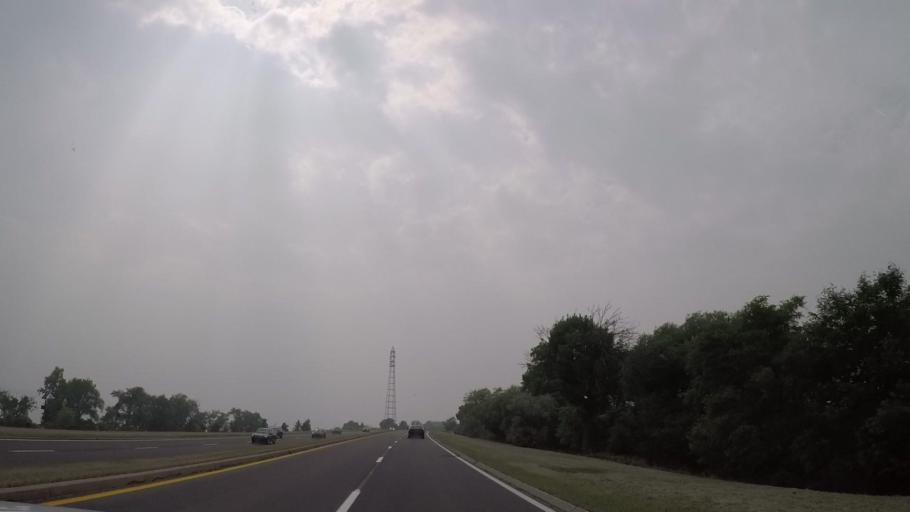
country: US
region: New York
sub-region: Niagara County
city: Niagara Falls
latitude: 43.0743
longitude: -79.0006
